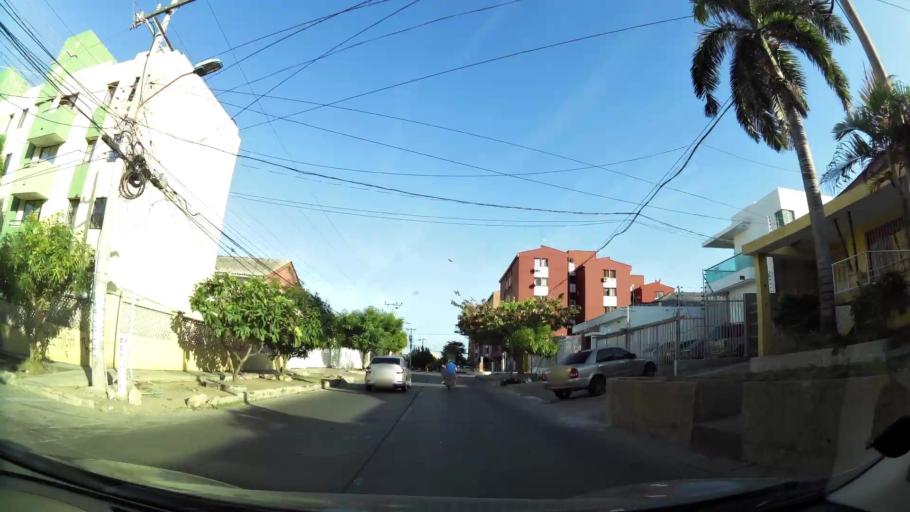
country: CO
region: Atlantico
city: Barranquilla
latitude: 10.9877
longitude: -74.8055
